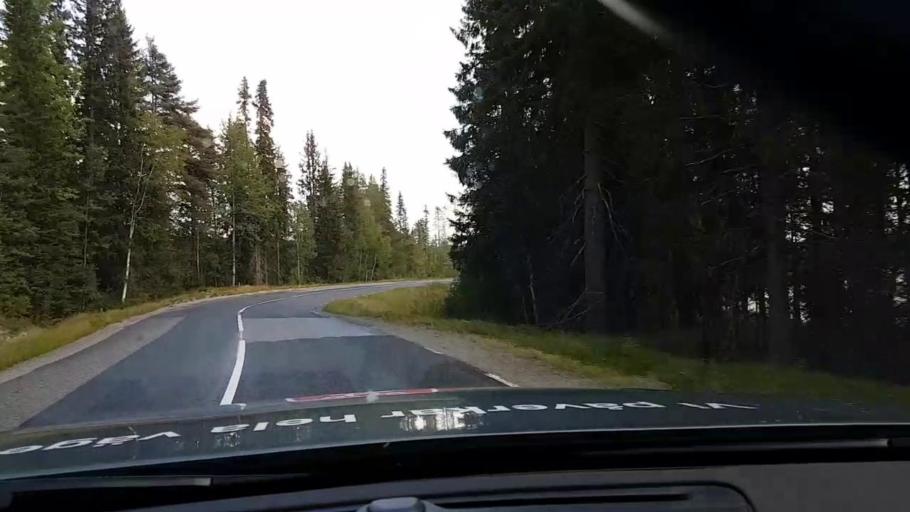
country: SE
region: Vaesterbotten
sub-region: Asele Kommun
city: Asele
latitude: 63.8356
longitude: 17.4403
